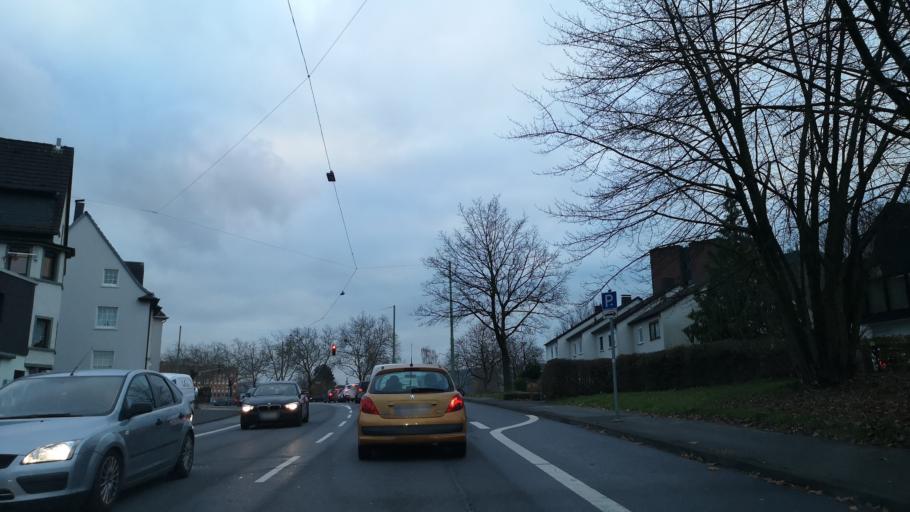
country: DE
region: North Rhine-Westphalia
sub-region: Regierungsbezirk Arnsberg
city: Hagen
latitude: 51.3686
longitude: 7.4747
